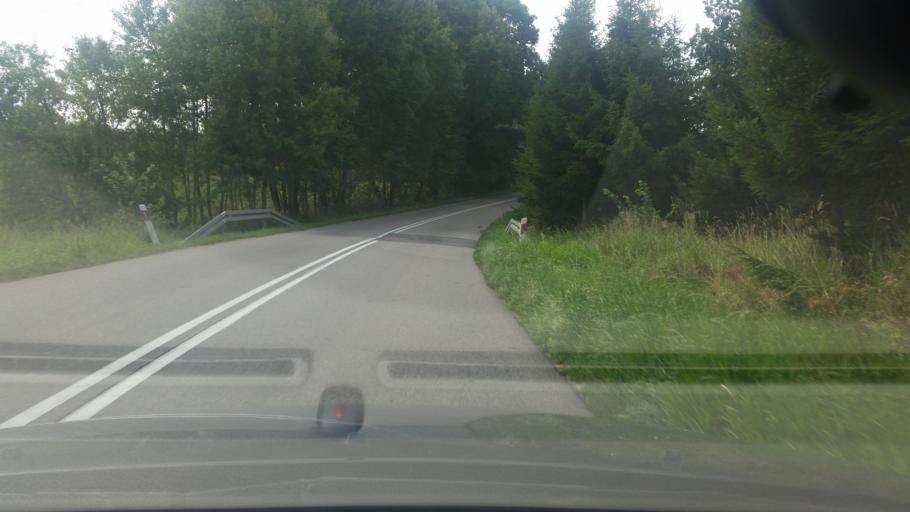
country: PL
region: Pomeranian Voivodeship
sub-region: Powiat leborski
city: Leba
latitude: 54.7467
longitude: 17.6624
